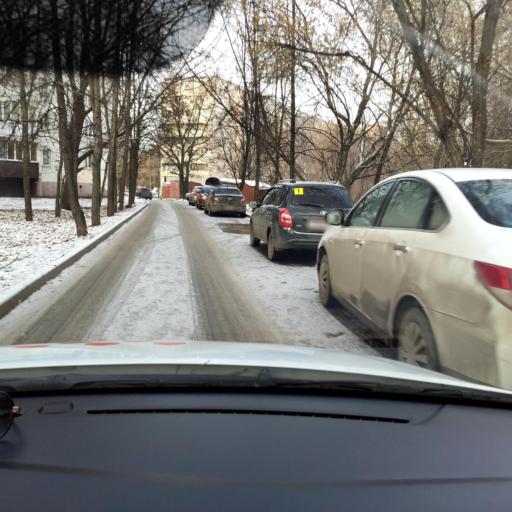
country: RU
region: Tatarstan
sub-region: Gorod Kazan'
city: Kazan
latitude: 55.7541
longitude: 49.2064
